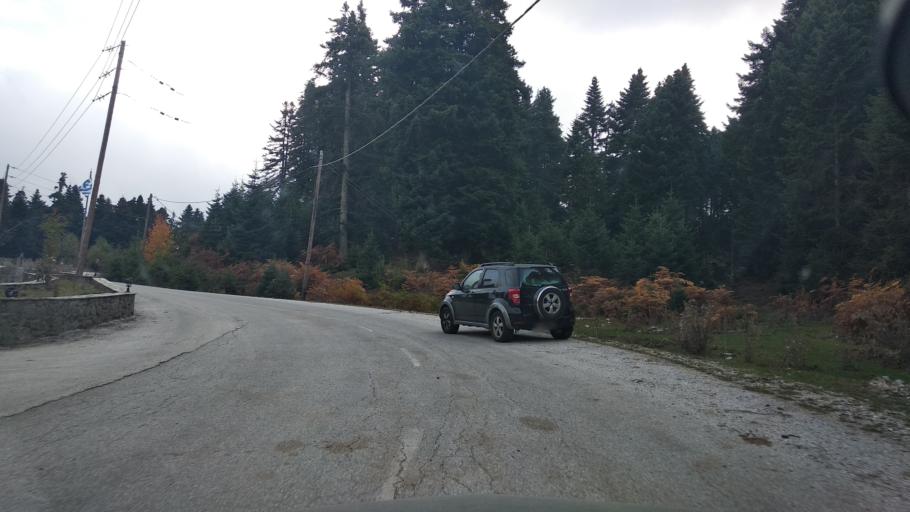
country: GR
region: Thessaly
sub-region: Trikala
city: Fiki
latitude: 39.5817
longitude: 21.4906
